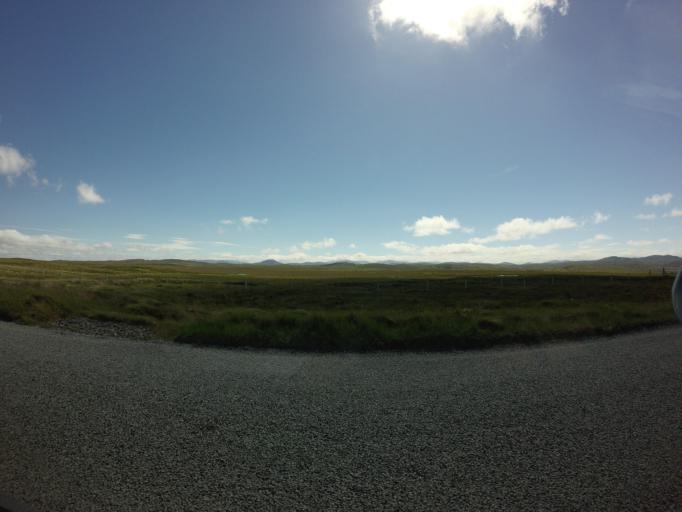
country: GB
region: Scotland
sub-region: Eilean Siar
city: Isle of Lewis
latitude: 58.1876
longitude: -6.6923
